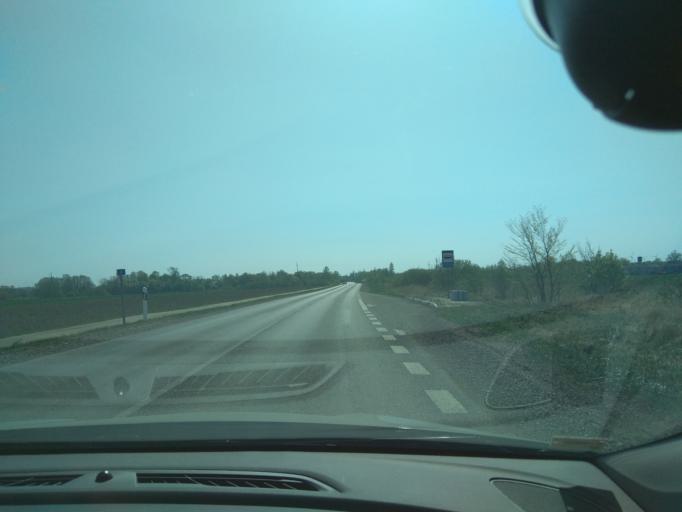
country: LT
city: Linkuva
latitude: 56.0321
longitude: 23.9487
